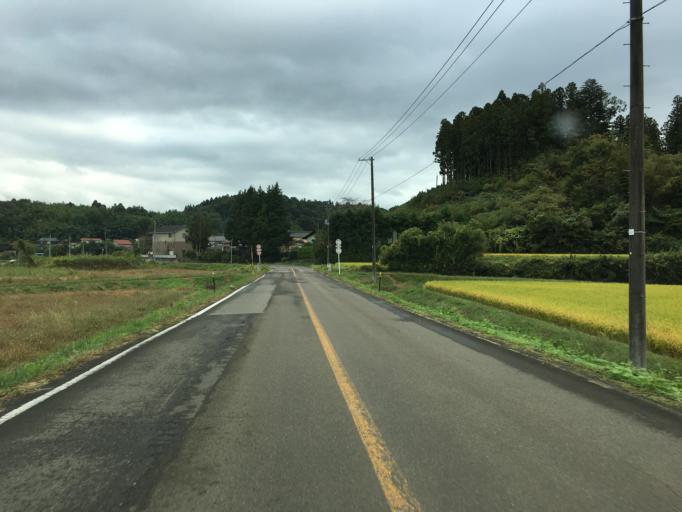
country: JP
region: Fukushima
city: Nihommatsu
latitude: 37.6159
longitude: 140.4378
